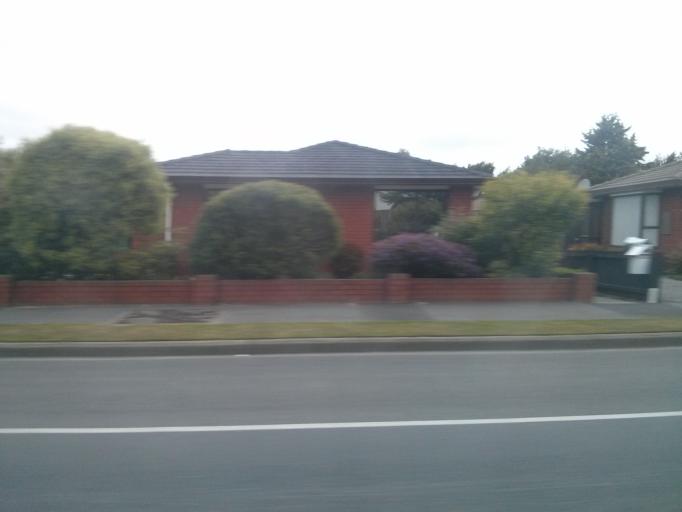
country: NZ
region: Canterbury
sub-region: Christchurch City
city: Christchurch
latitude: -43.4821
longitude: 172.6166
